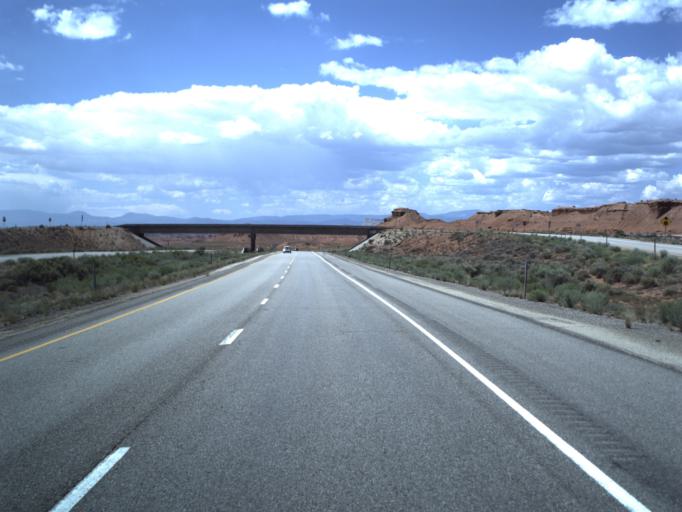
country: US
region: Utah
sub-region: Emery County
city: Ferron
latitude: 38.8439
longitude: -111.0618
